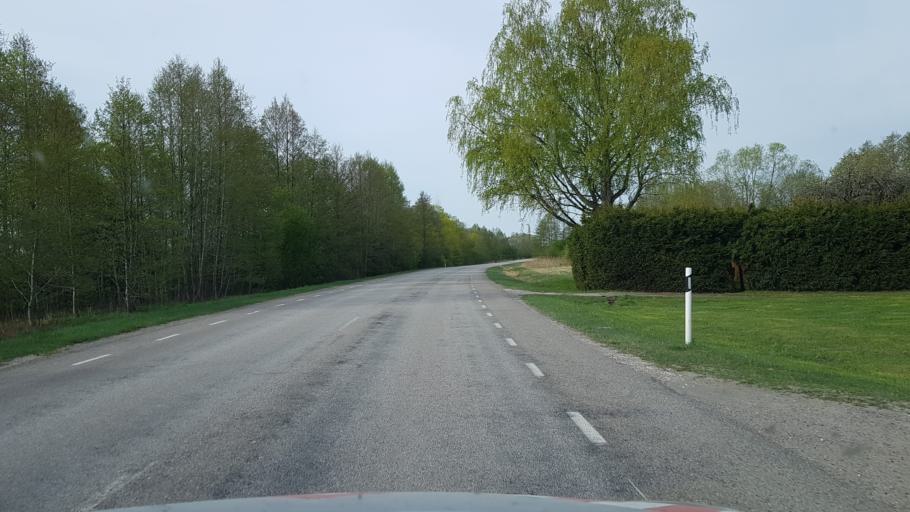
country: EE
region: Paernumaa
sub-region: Audru vald
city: Audru
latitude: 58.4010
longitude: 24.2987
